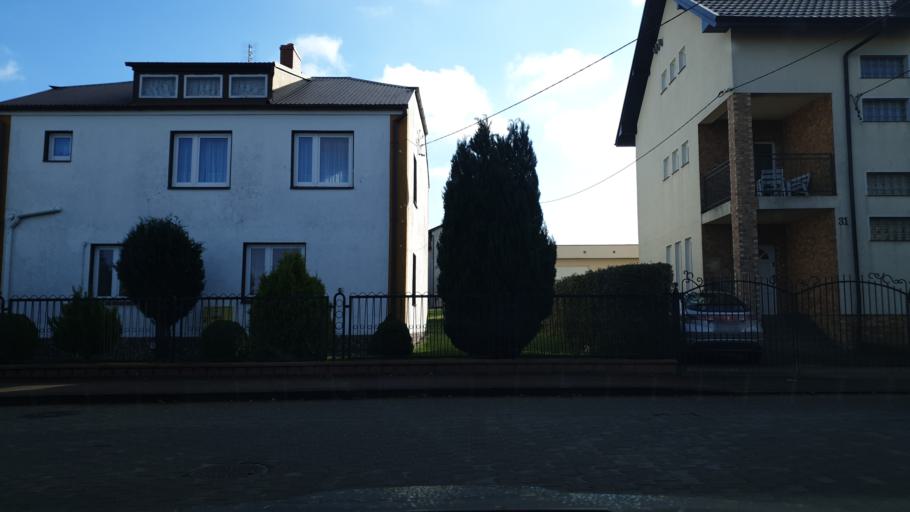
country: PL
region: Pomeranian Voivodeship
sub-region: Powiat pucki
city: Jastrzebia Gora
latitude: 54.8235
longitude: 18.2399
